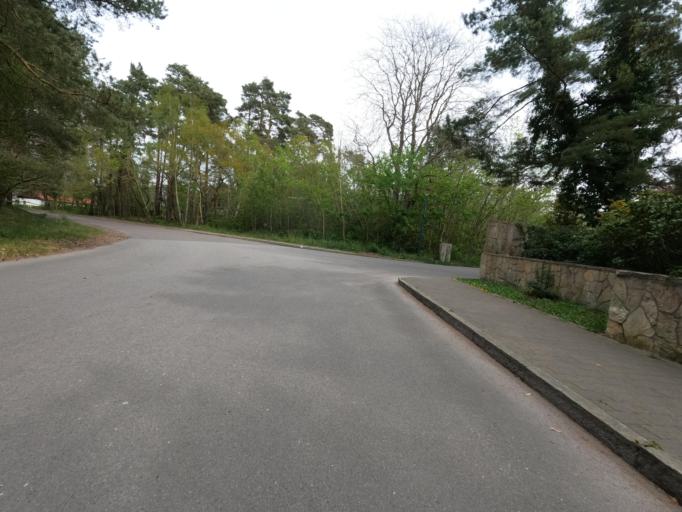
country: DE
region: Mecklenburg-Vorpommern
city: Ostseebad Prerow
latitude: 54.4455
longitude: 12.5503
